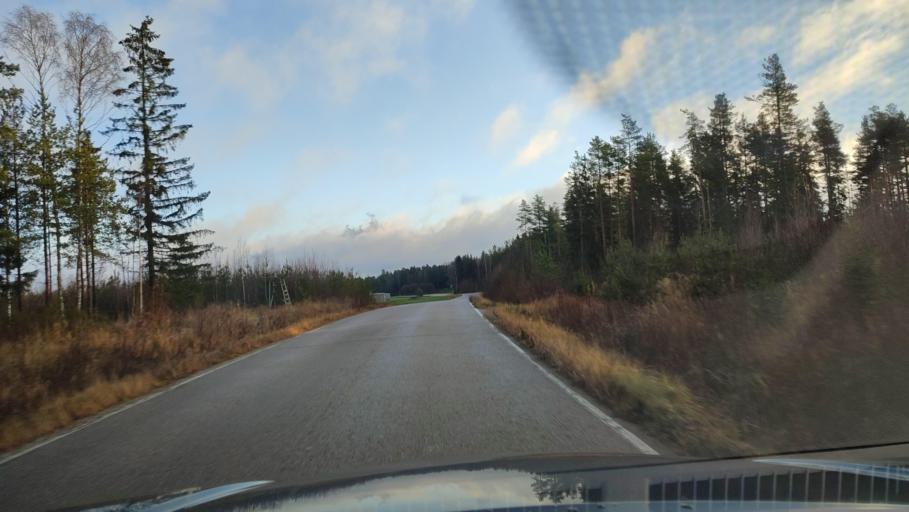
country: FI
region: Ostrobothnia
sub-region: Sydosterbotten
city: Naerpes
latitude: 62.4431
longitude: 21.3972
